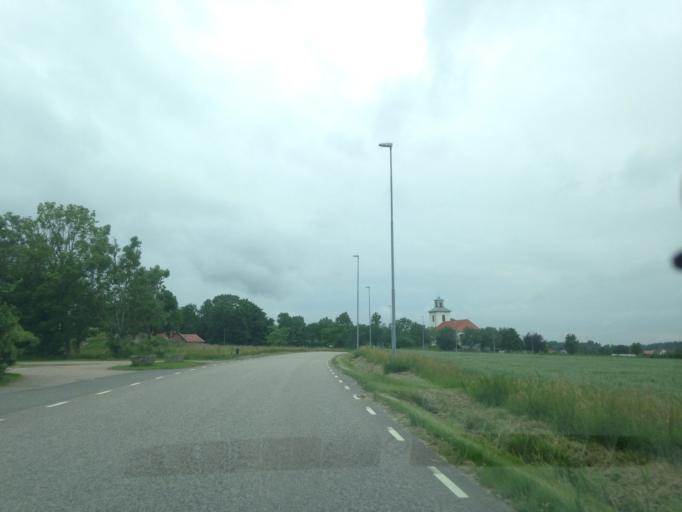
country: SE
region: Vaestra Goetaland
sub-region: Kungalvs Kommun
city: Kode
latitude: 57.8175
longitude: 11.8426
